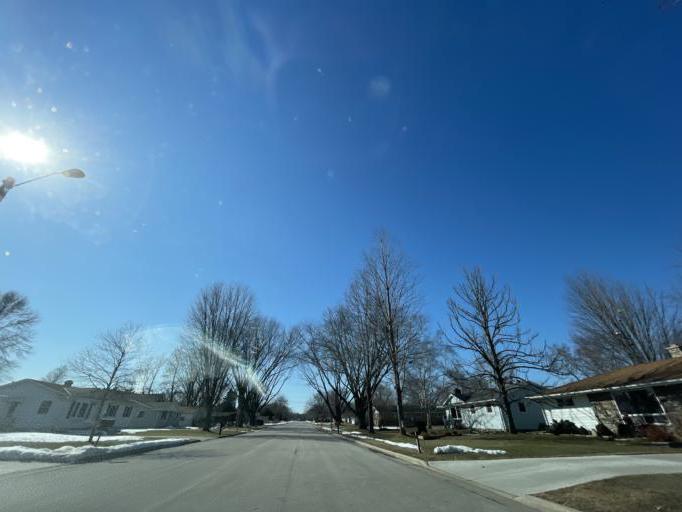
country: US
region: Wisconsin
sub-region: Brown County
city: Howard
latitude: 44.5685
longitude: -88.0834
